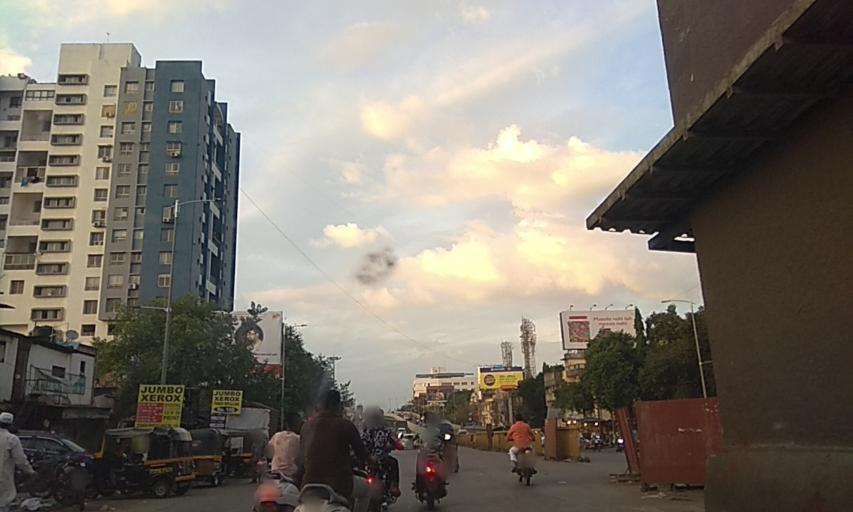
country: IN
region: Maharashtra
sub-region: Pune Division
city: Pune
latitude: 18.4934
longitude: 73.8577
